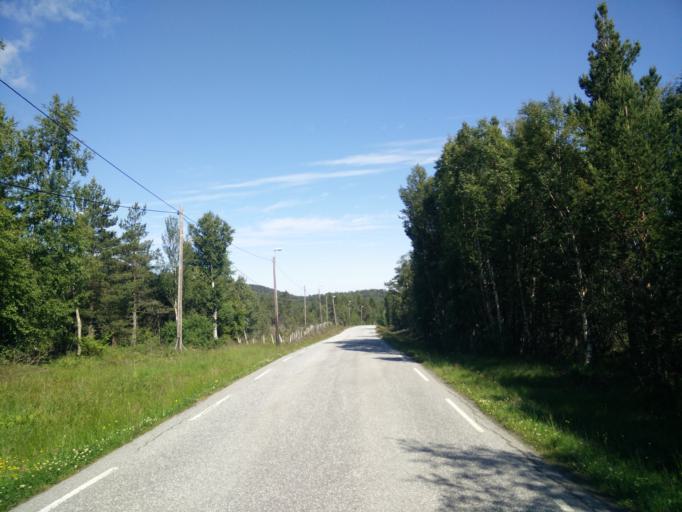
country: NO
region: More og Romsdal
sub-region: Kristiansund
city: Rensvik
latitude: 63.0637
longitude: 7.8688
